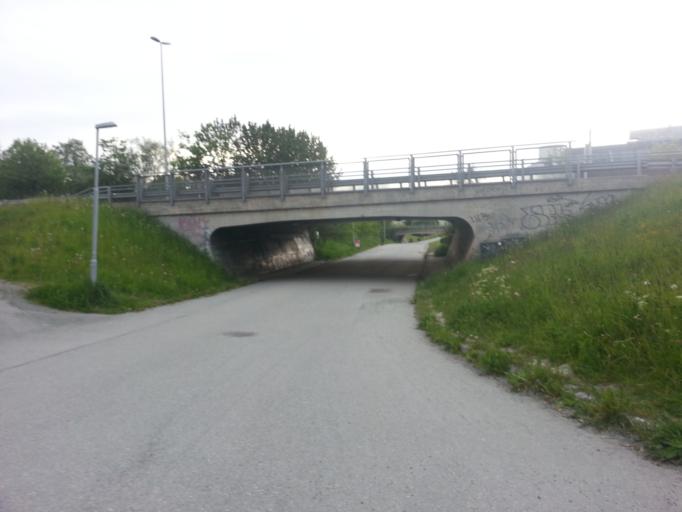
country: NO
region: Sor-Trondelag
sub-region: Trondheim
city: Trondheim
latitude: 63.4110
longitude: 10.4458
